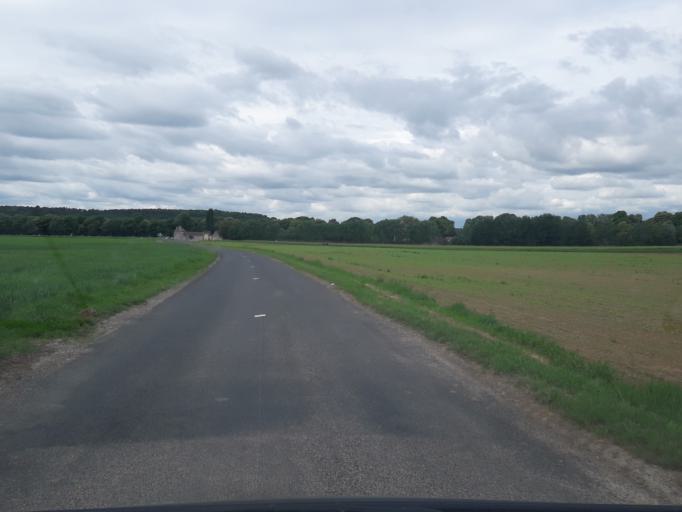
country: FR
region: Ile-de-France
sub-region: Departement de l'Essonne
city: Boissy-le-Cutte
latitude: 48.4205
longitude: 2.2840
